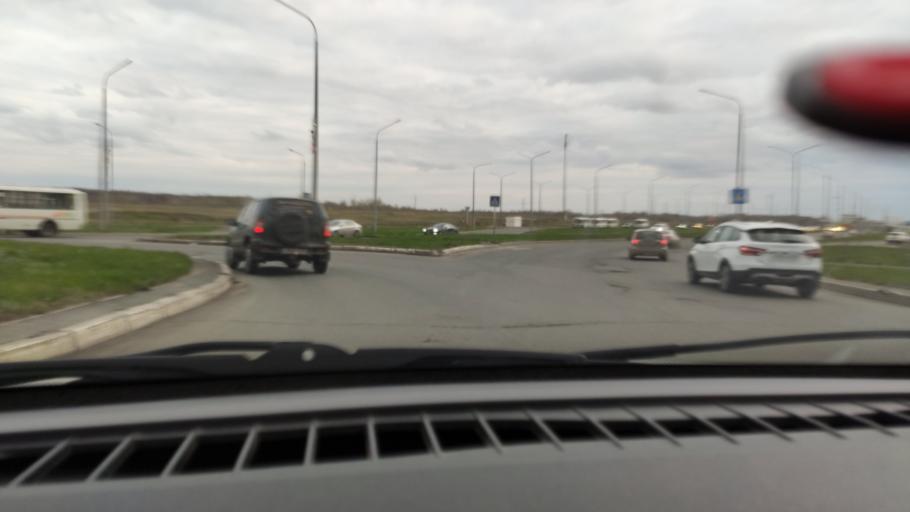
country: RU
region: Orenburg
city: Orenburg
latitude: 51.8103
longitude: 55.1794
